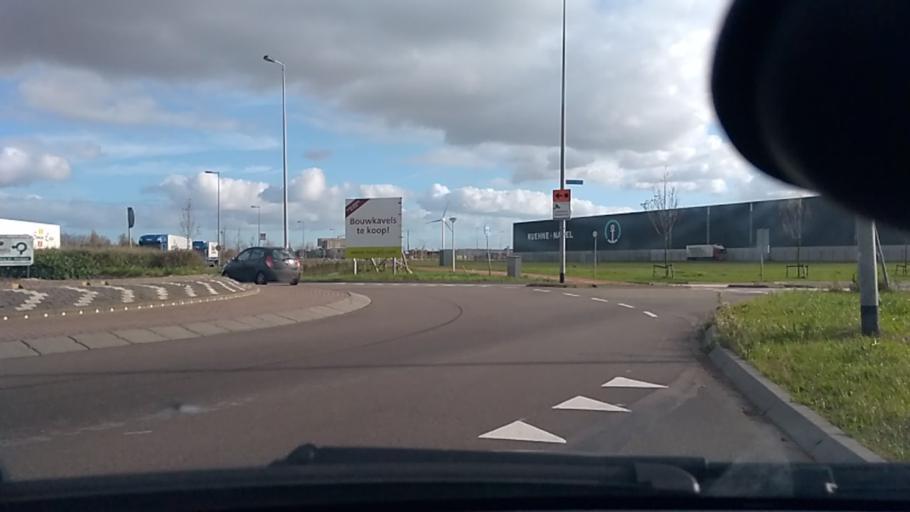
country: NL
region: North Holland
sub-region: Gemeente Zaanstad
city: Zaanstad
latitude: 52.4315
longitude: 4.7742
